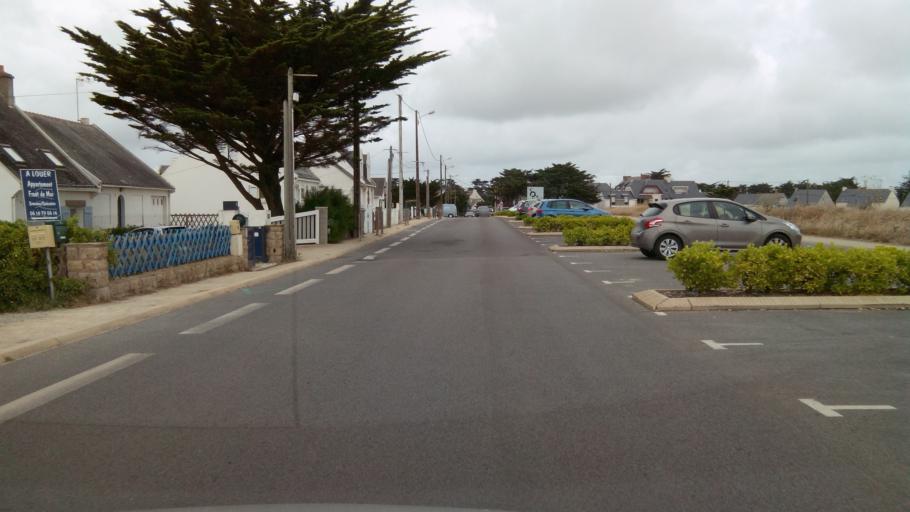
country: FR
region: Pays de la Loire
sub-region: Departement de la Loire-Atlantique
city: Batz-sur-Mer
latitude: 47.2789
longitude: -2.4933
